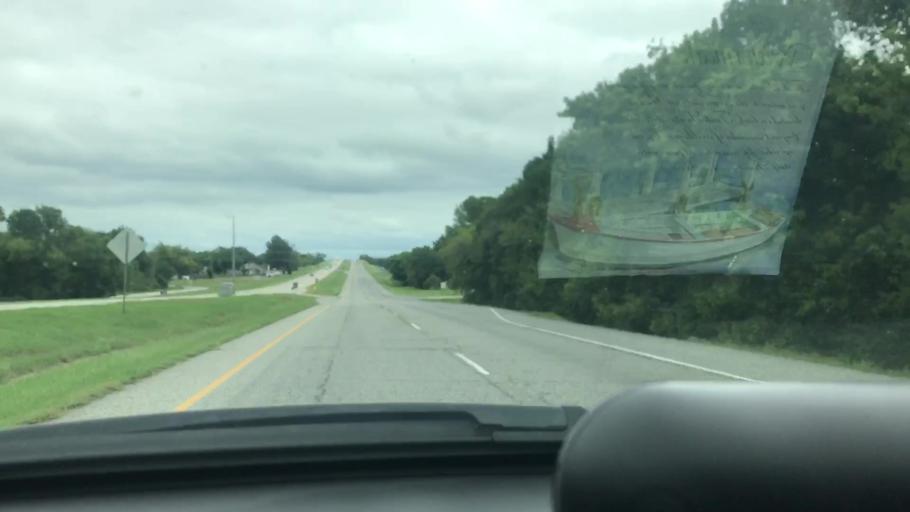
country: US
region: Oklahoma
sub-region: Wagoner County
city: Wagoner
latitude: 35.9706
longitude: -95.3876
